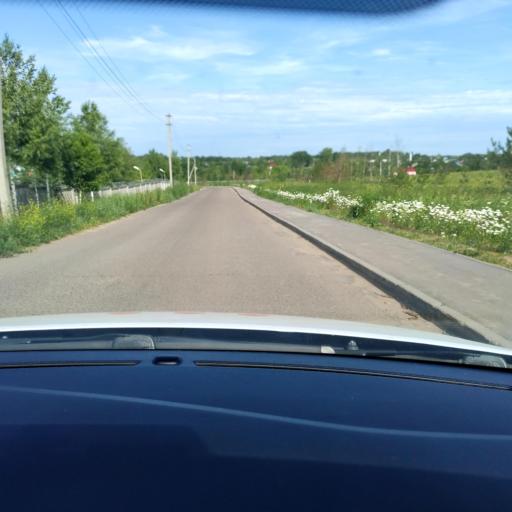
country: RU
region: Tatarstan
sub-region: Gorod Kazan'
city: Kazan
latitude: 55.8922
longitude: 49.0902
